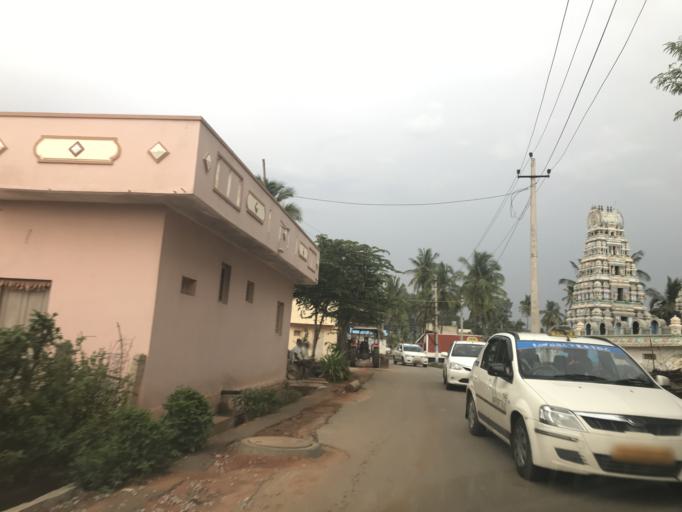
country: IN
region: Karnataka
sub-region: Bangalore Rural
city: Devanhalli
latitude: 13.1792
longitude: 77.6657
